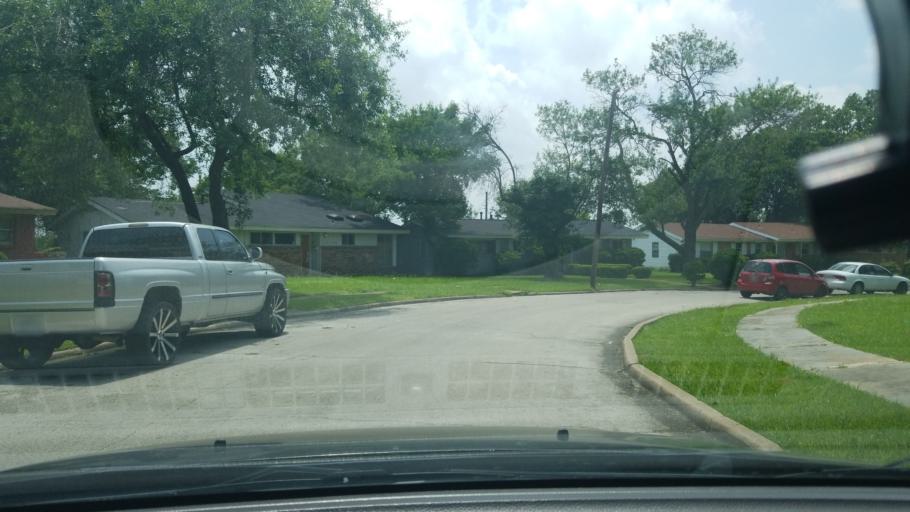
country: US
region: Texas
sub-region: Dallas County
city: Mesquite
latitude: 32.7943
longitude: -96.6370
